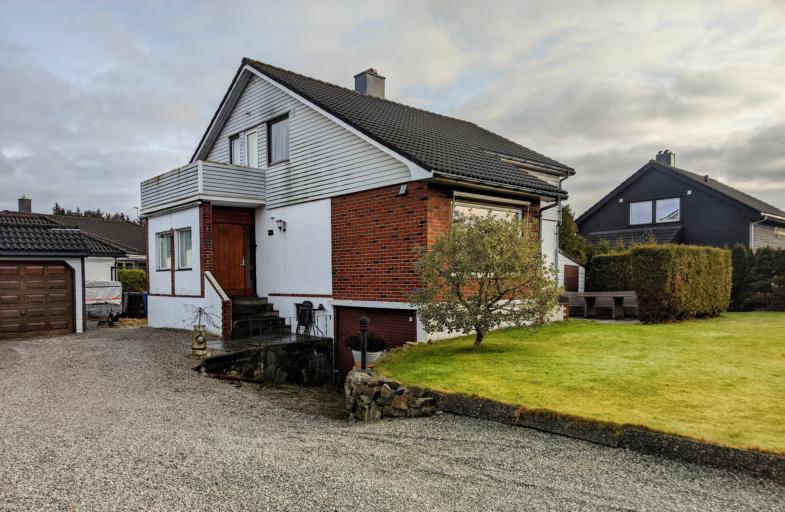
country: NO
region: Rogaland
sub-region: Sandnes
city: Sandnes
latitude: 58.8377
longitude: 5.7426
